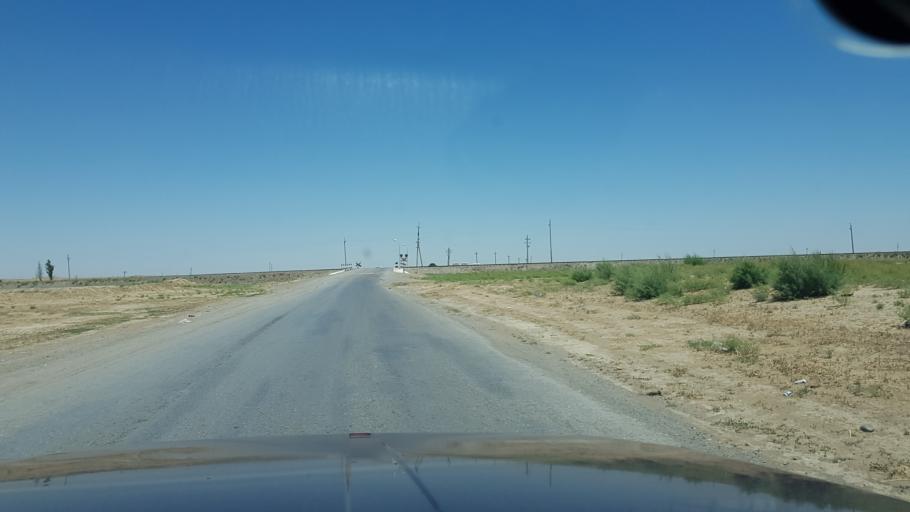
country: TM
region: Ahal
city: Annau
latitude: 37.8474
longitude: 58.7135
